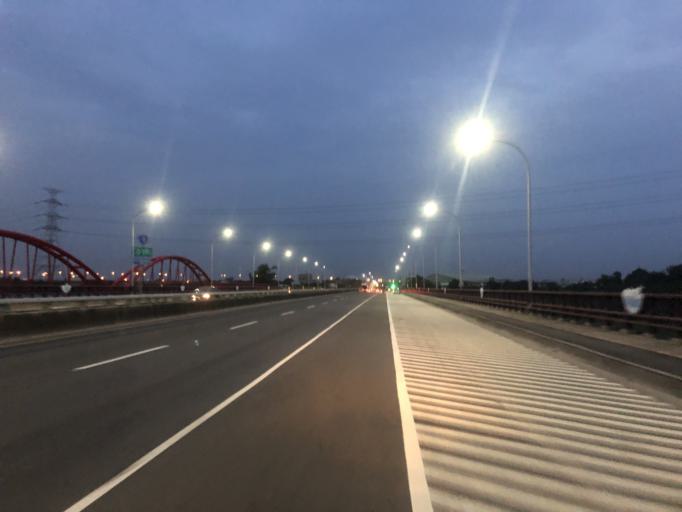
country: TW
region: Taiwan
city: Yujing
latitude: 23.1547
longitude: 120.3375
